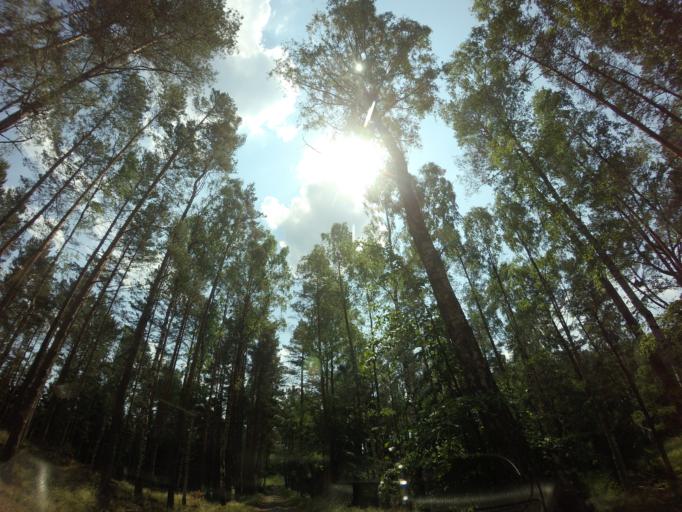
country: PL
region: West Pomeranian Voivodeship
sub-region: Powiat choszczenski
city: Bierzwnik
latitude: 53.0974
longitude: 15.7130
